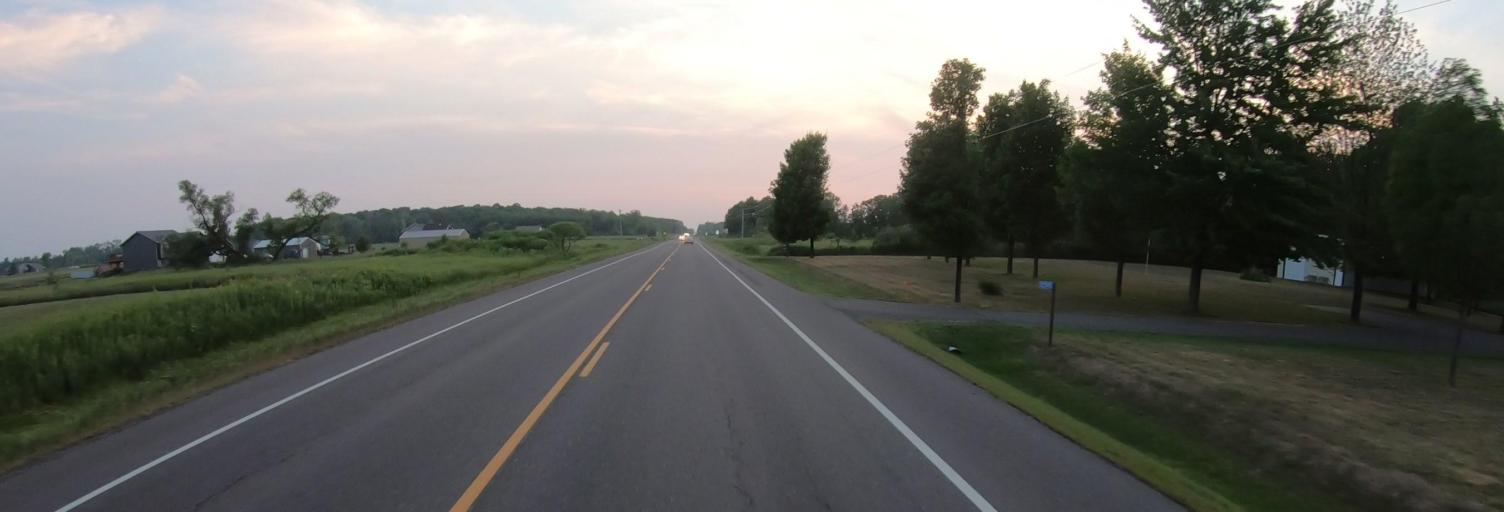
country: US
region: Minnesota
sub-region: Pine County
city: Rock Creek
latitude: 45.7735
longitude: -92.8517
